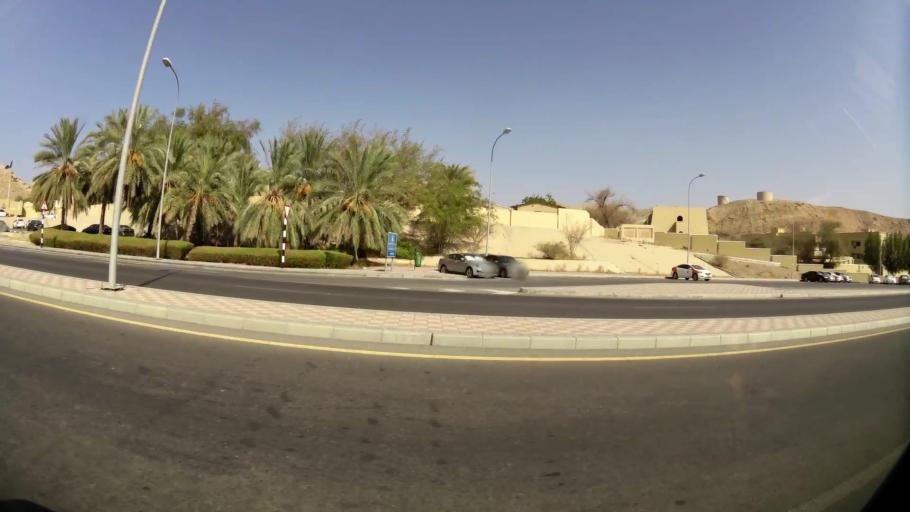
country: OM
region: Muhafazat Masqat
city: Muscat
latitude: 23.6163
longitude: 58.5186
